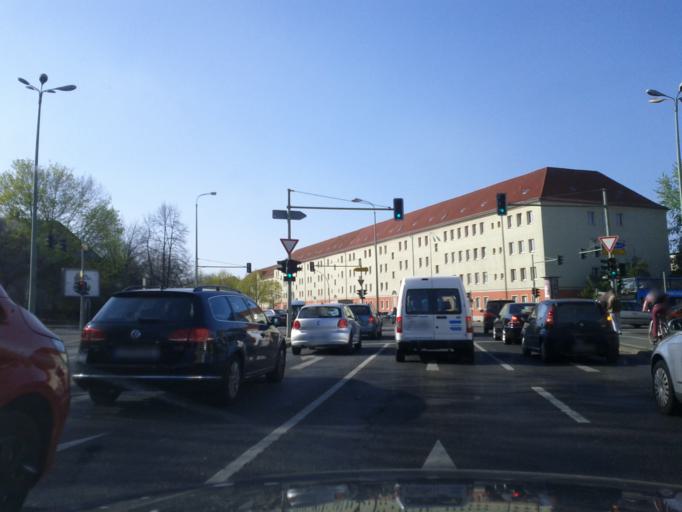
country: DE
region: Berlin
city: Friedrichshain Bezirk
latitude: 52.5368
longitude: 13.4499
